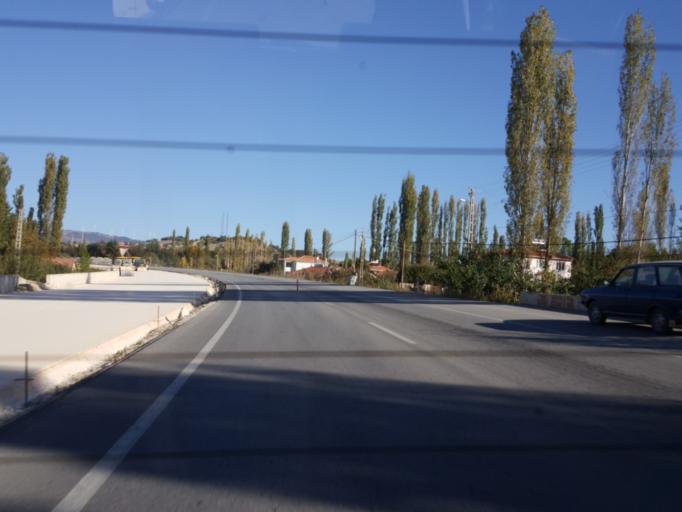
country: TR
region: Amasya
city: Ezinepazari
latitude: 40.5466
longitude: 36.1518
